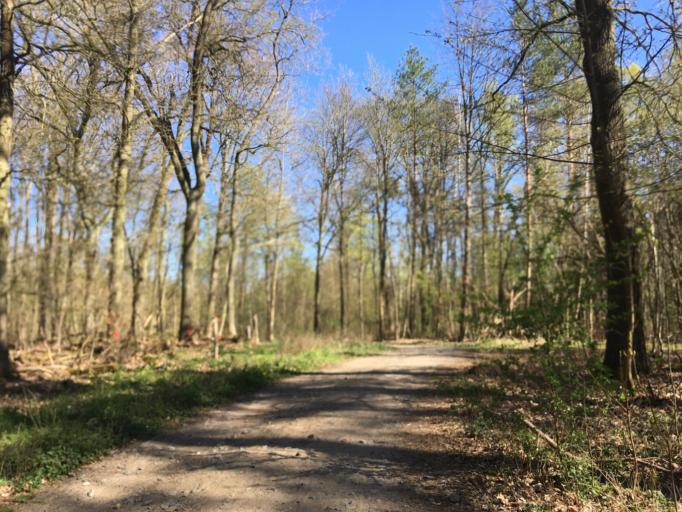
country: DE
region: Berlin
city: Buch
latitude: 52.6554
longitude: 13.4781
